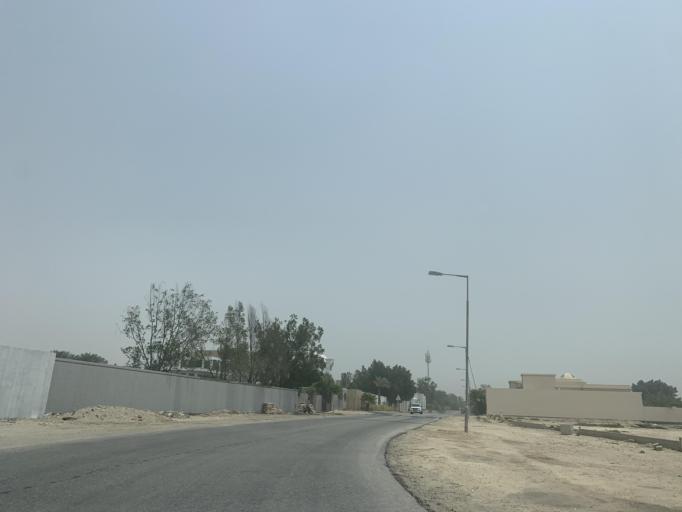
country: BH
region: Central Governorate
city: Madinat Hamad
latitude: 26.1676
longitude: 50.4725
